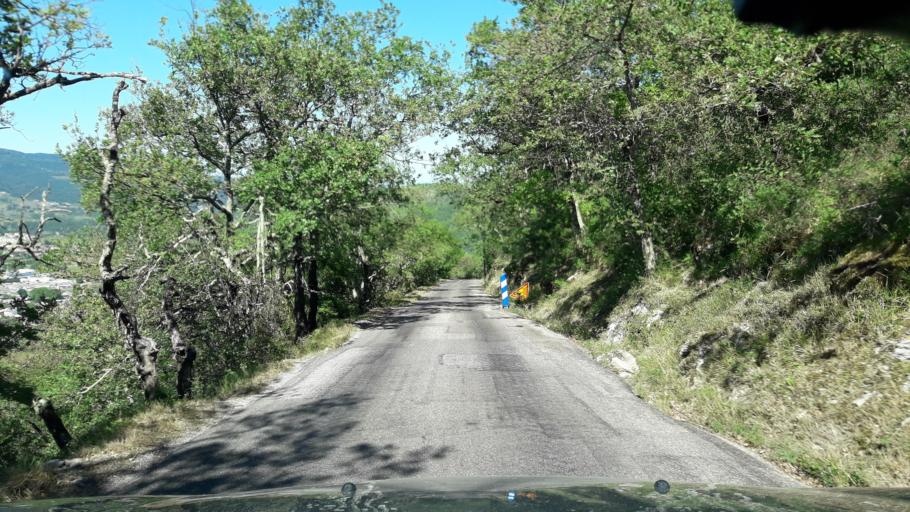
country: FR
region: Rhone-Alpes
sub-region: Departement de l'Ardeche
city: Privas
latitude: 44.7122
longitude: 4.5968
